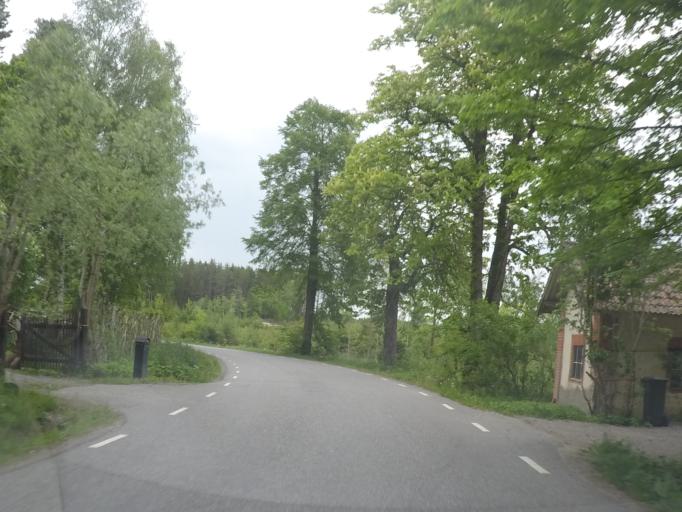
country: SE
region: Soedermanland
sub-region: Nykopings Kommun
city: Svalsta
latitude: 58.8184
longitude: 16.9065
